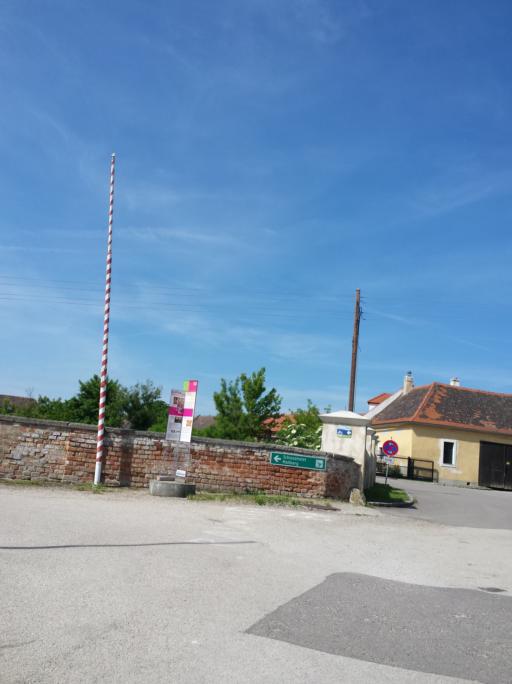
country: AT
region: Lower Austria
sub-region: Politischer Bezirk Hollabrunn
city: Mailberg
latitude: 48.6711
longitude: 16.1822
